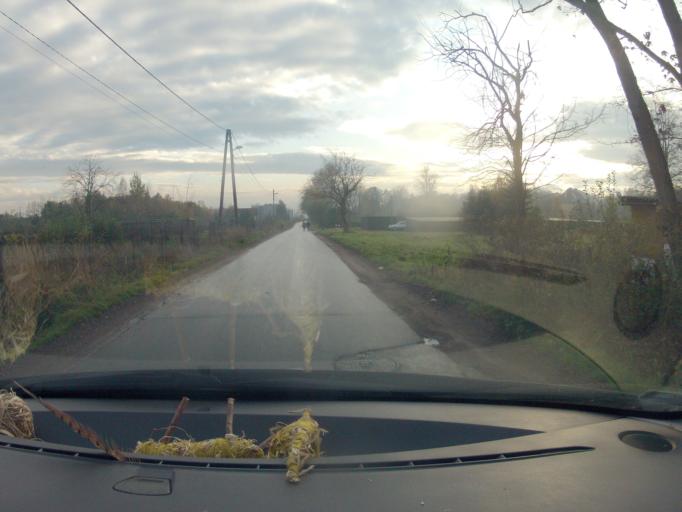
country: PL
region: Lesser Poland Voivodeship
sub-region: Krakow
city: Sidzina
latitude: 50.0048
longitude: 19.8898
